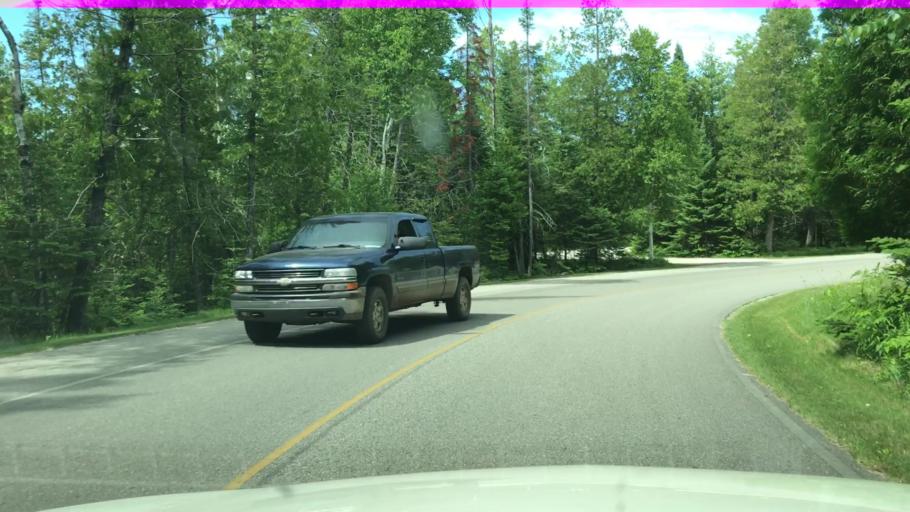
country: US
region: Michigan
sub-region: Schoolcraft County
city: Manistique
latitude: 45.9420
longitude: -86.3339
